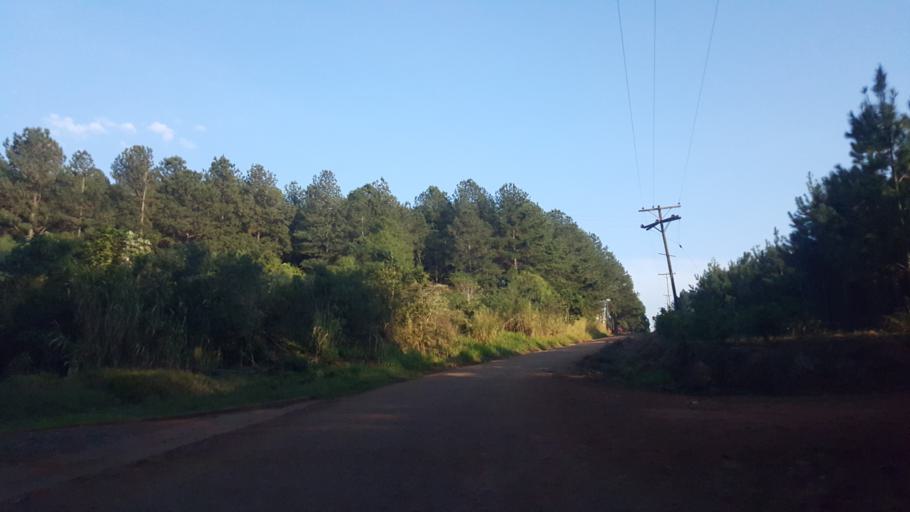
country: AR
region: Misiones
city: Capiovi
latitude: -26.8893
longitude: -55.0592
